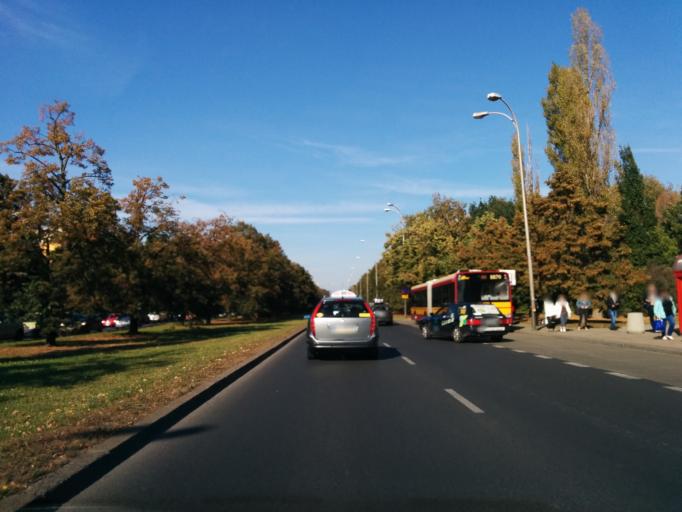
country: PL
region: Masovian Voivodeship
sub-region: Warszawa
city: Ochota
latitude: 52.1987
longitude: 20.9841
